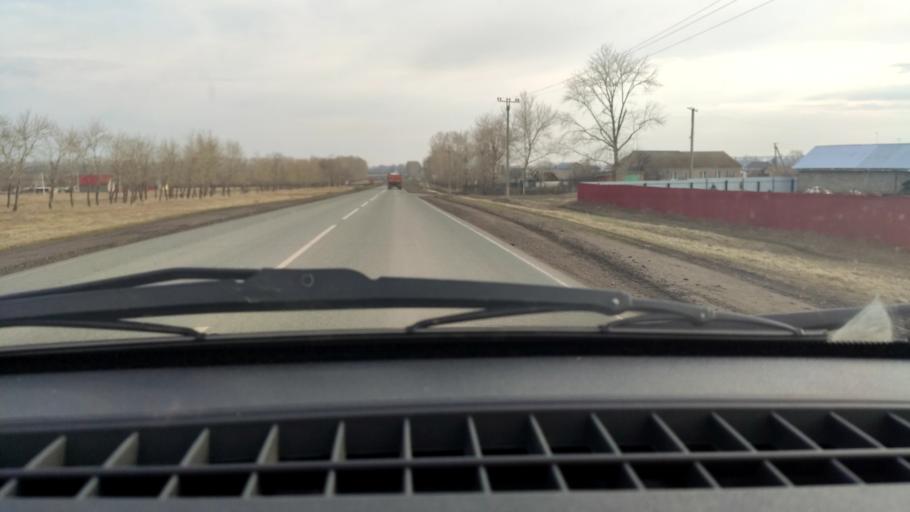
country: RU
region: Bashkortostan
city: Davlekanovo
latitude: 54.3871
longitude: 55.1994
